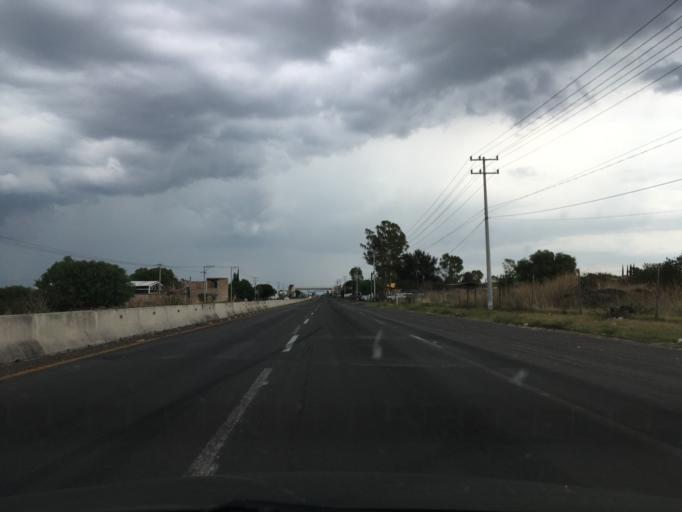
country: MX
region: Guanajuato
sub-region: Celaya
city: El Sauz (El Sauz de Villasenor)
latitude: 20.3914
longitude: -100.7908
